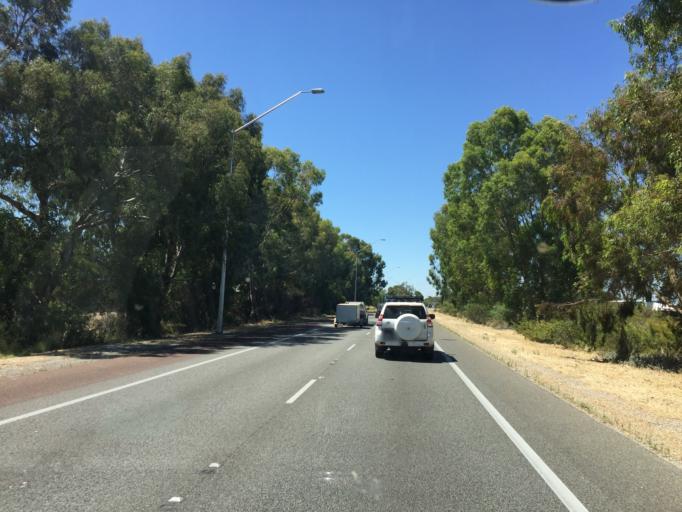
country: AU
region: Western Australia
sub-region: Canning
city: East Cannington
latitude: -32.0148
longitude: 115.9717
